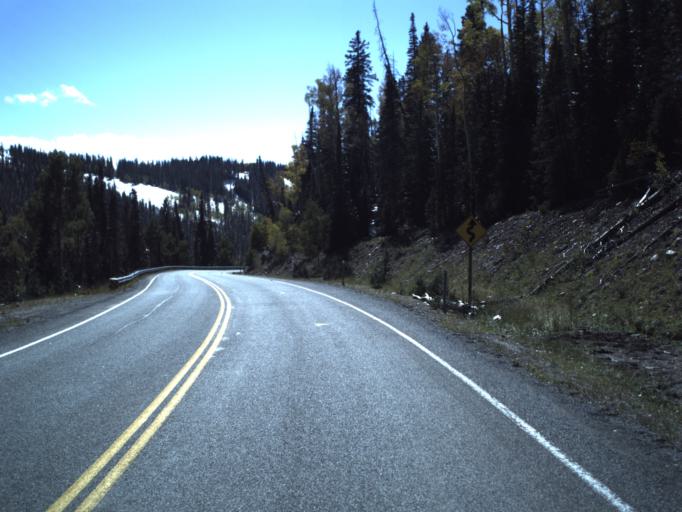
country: US
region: Utah
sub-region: Piute County
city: Junction
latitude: 38.3253
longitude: -112.3747
